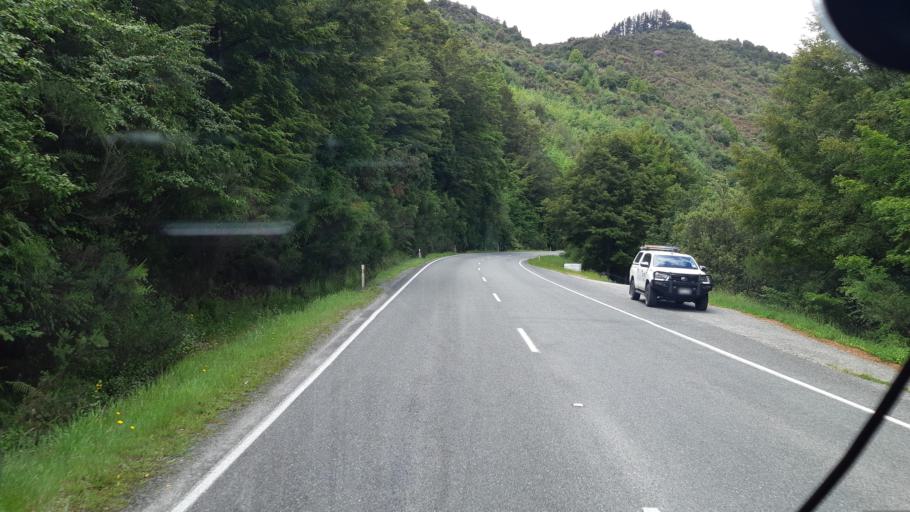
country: NZ
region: West Coast
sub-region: Buller District
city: Westport
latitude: -42.1201
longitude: 171.8725
